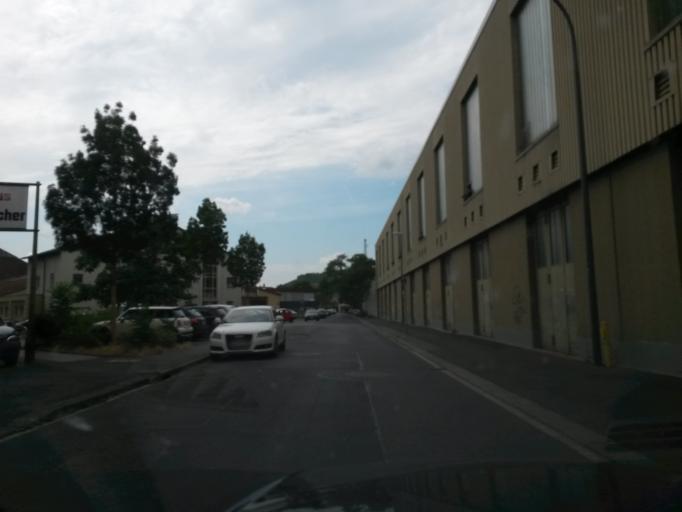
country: DE
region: Bavaria
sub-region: Regierungsbezirk Unterfranken
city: Wuerzburg
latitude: 49.8026
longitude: 9.9252
